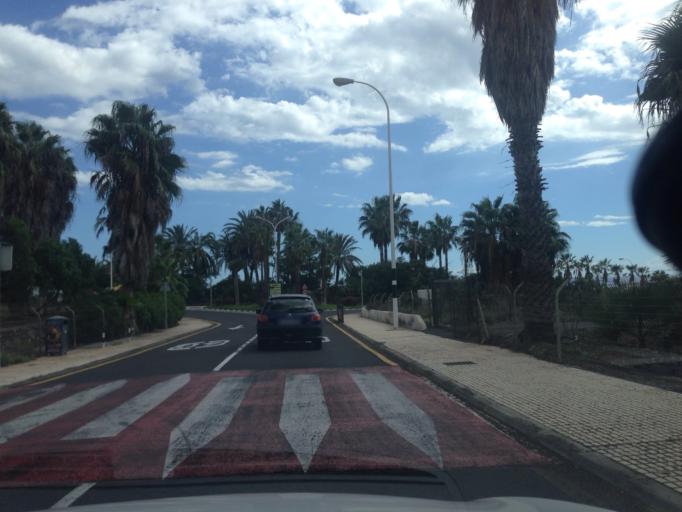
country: ES
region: Canary Islands
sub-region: Provincia de Santa Cruz de Tenerife
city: Las Rosas
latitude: 28.0348
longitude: -16.6113
